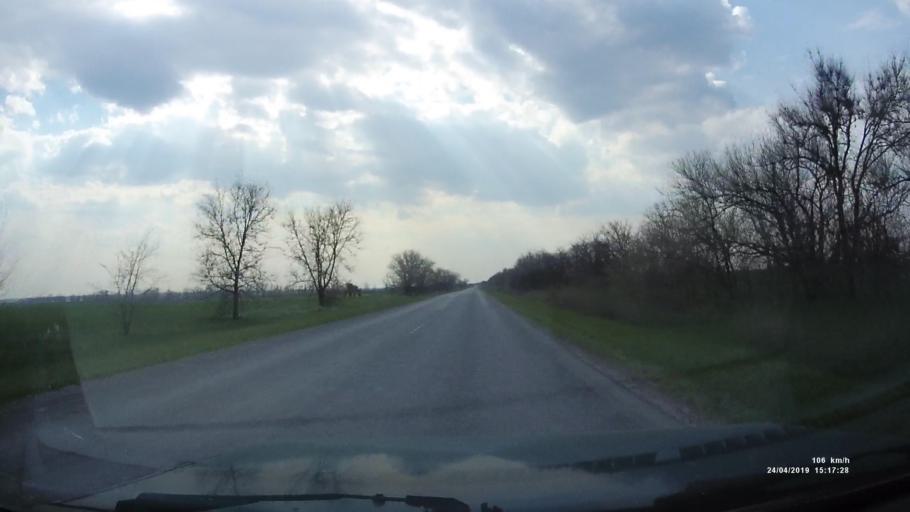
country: RU
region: Rostov
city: Remontnoye
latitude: 46.5465
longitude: 43.1890
